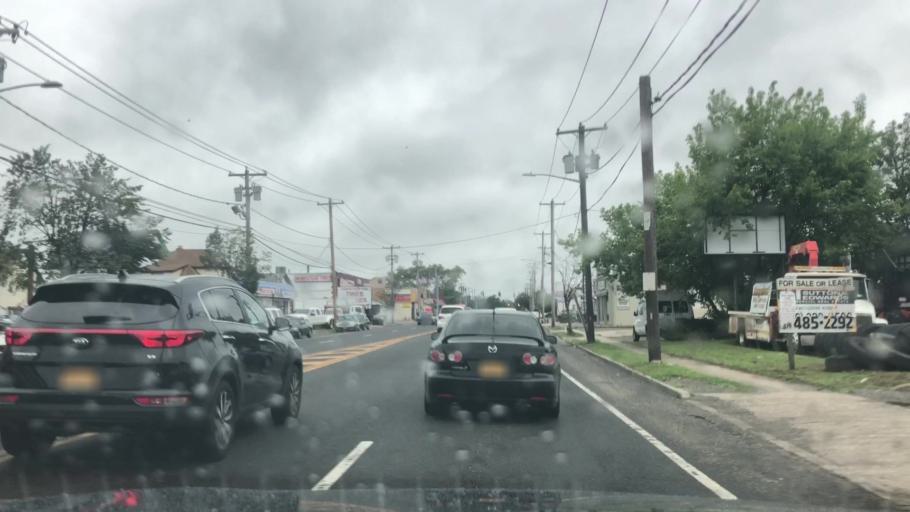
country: US
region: New York
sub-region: Nassau County
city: West Hempstead
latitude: 40.7051
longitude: -73.6469
